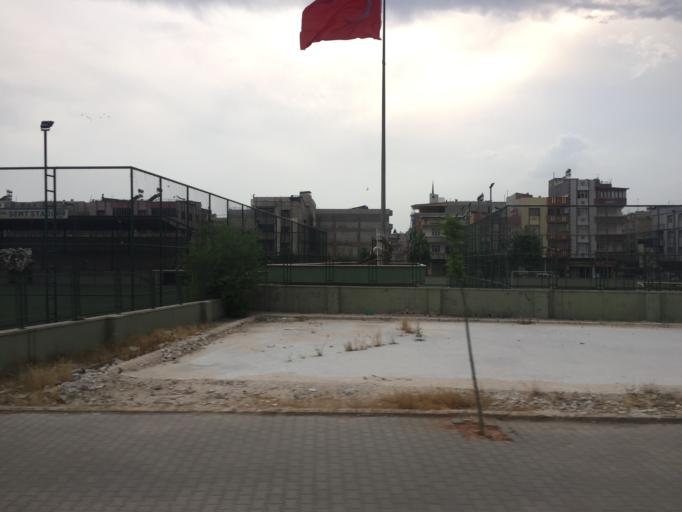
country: TR
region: Gaziantep
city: Gaziantep
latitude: 37.0652
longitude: 37.4148
